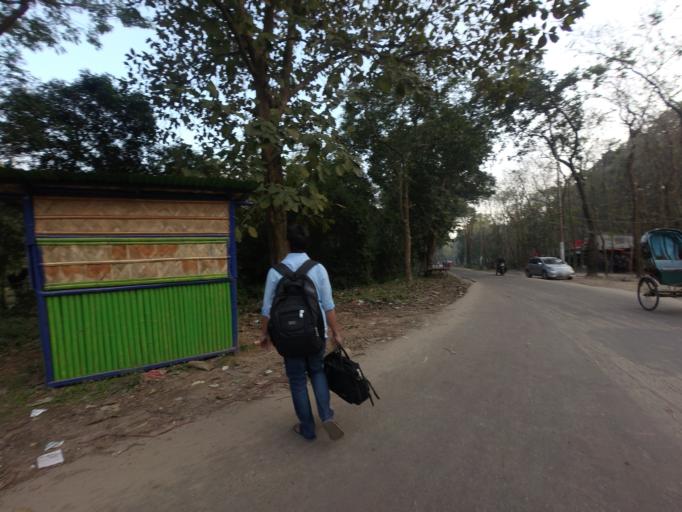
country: BD
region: Chittagong
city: Chittagong
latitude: 22.4705
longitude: 91.7871
